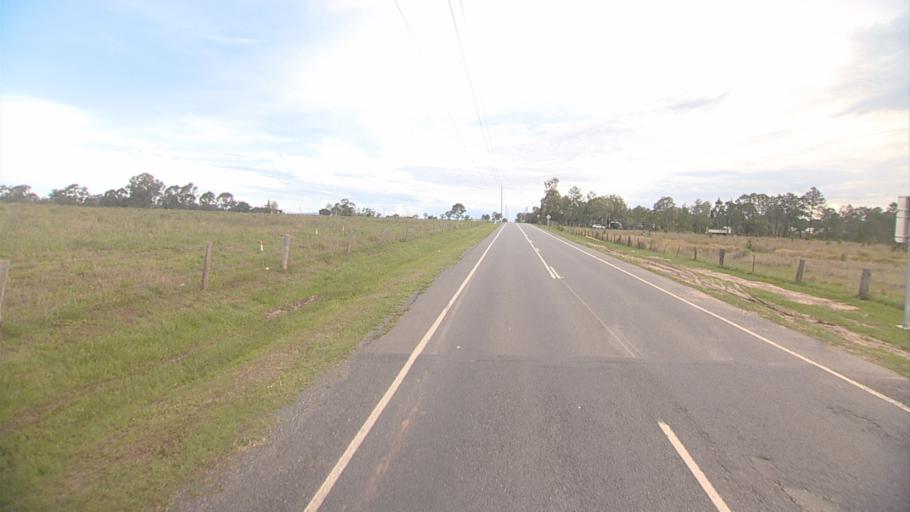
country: AU
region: Queensland
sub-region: Logan
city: Waterford West
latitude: -27.7056
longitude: 153.1172
